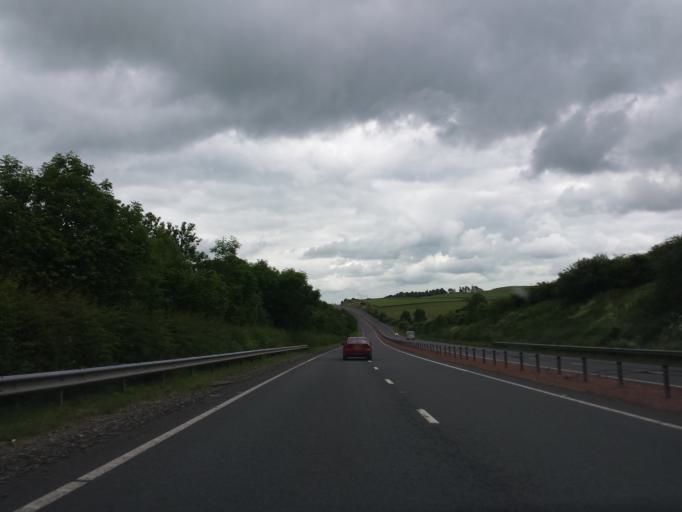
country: GB
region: Scotland
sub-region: Dumfries and Galloway
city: Dumfries
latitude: 55.0584
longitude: -3.7052
